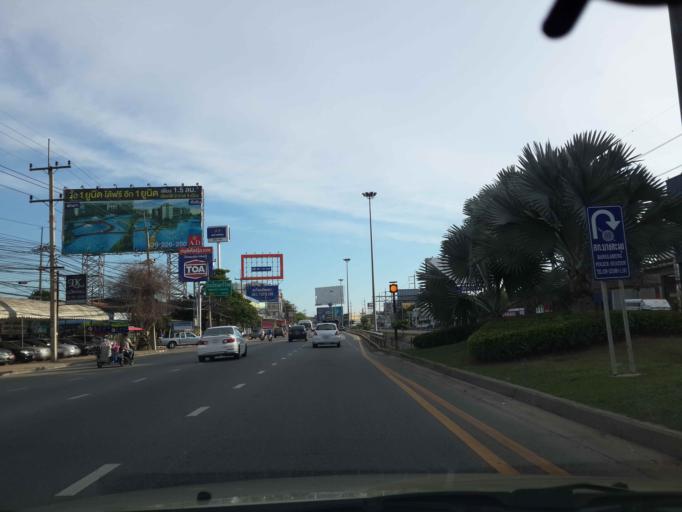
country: TH
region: Chon Buri
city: Phatthaya
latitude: 12.9750
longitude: 100.9141
